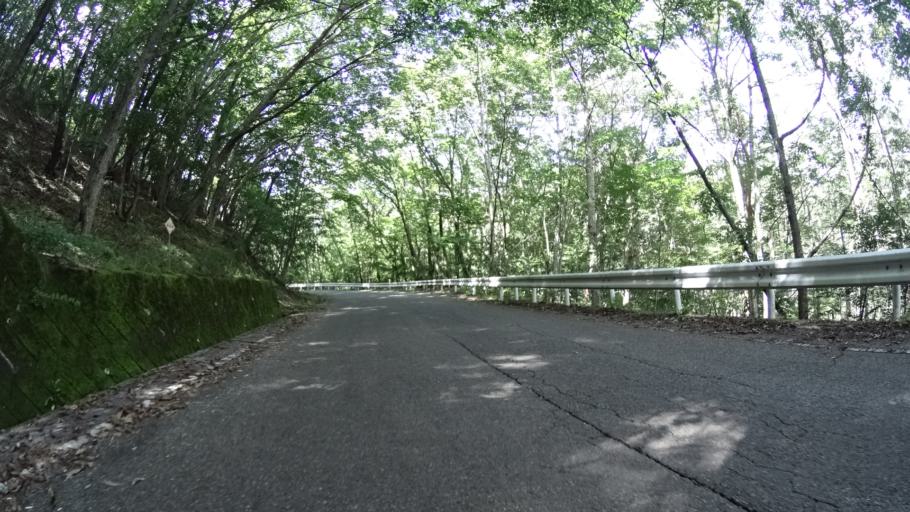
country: JP
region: Yamanashi
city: Nirasaki
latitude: 35.9062
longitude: 138.5424
